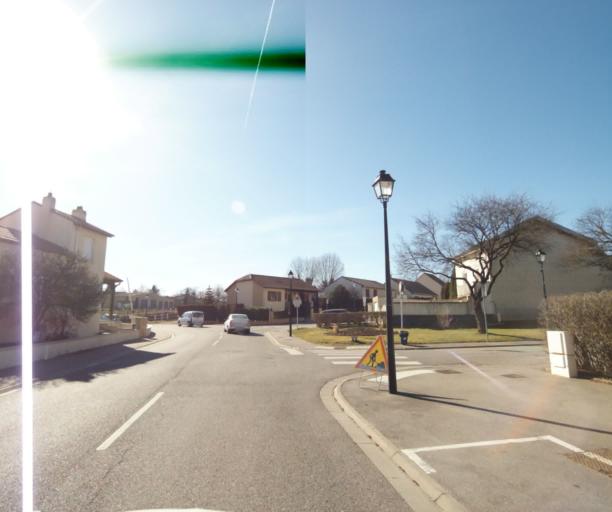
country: FR
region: Lorraine
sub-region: Departement de Meurthe-et-Moselle
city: Ludres
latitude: 48.6193
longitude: 6.1628
